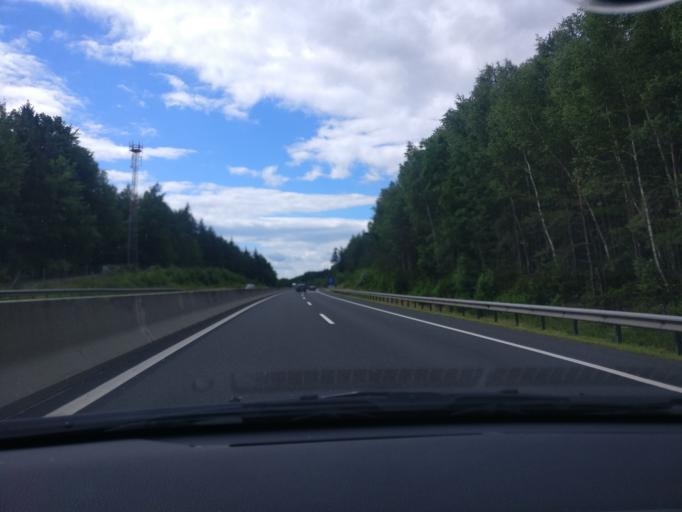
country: AT
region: Styria
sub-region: Politischer Bezirk Hartberg-Fuerstenfeld
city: Pinggau
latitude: 47.4021
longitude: 16.0814
